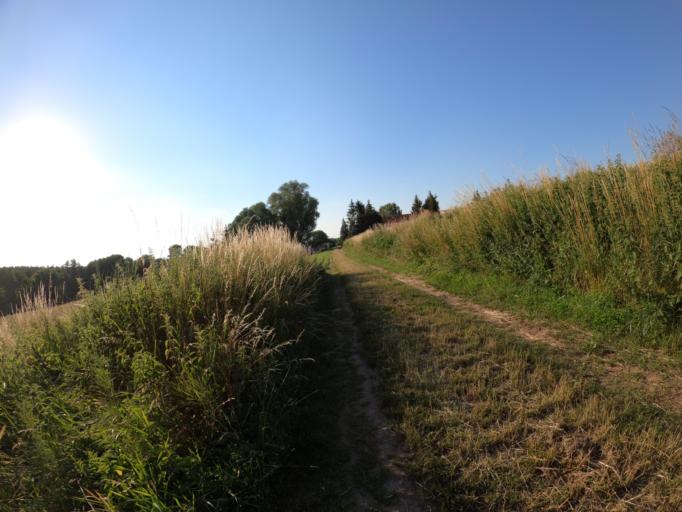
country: DE
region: Brandenburg
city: Tantow
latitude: 53.2504
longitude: 14.3643
